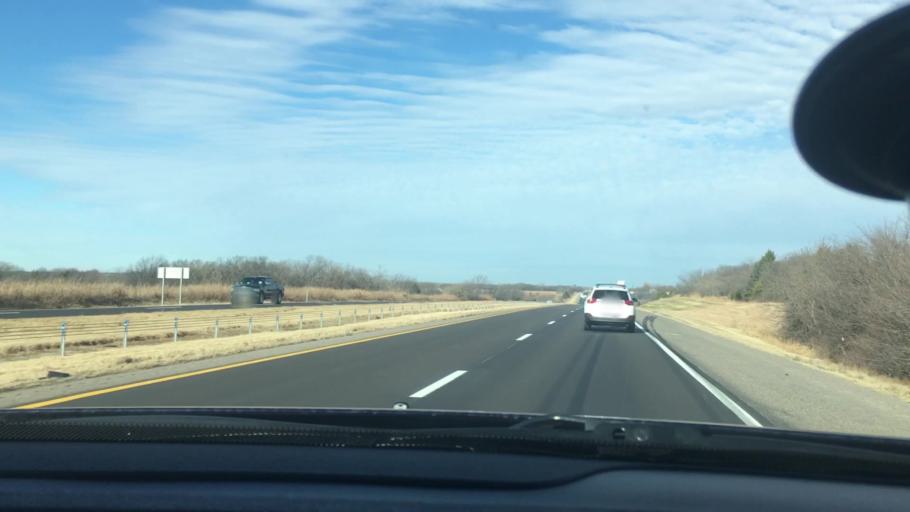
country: US
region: Oklahoma
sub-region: Cleveland County
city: Noble
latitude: 35.0975
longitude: -97.4251
